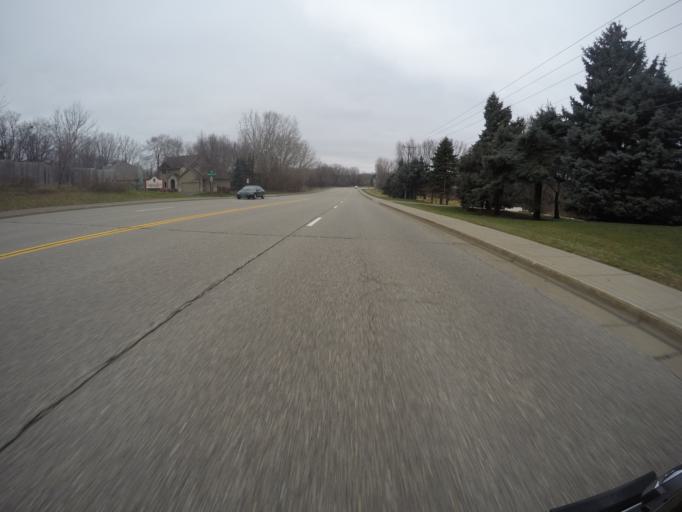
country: US
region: Minnesota
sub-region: Hennepin County
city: Eden Prairie
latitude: 44.8847
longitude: -93.4475
